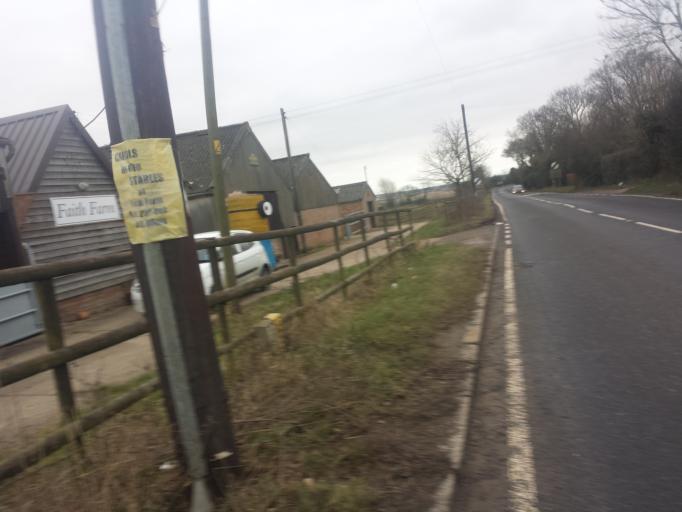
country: GB
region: England
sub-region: Essex
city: Little Clacton
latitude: 51.8797
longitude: 1.1680
